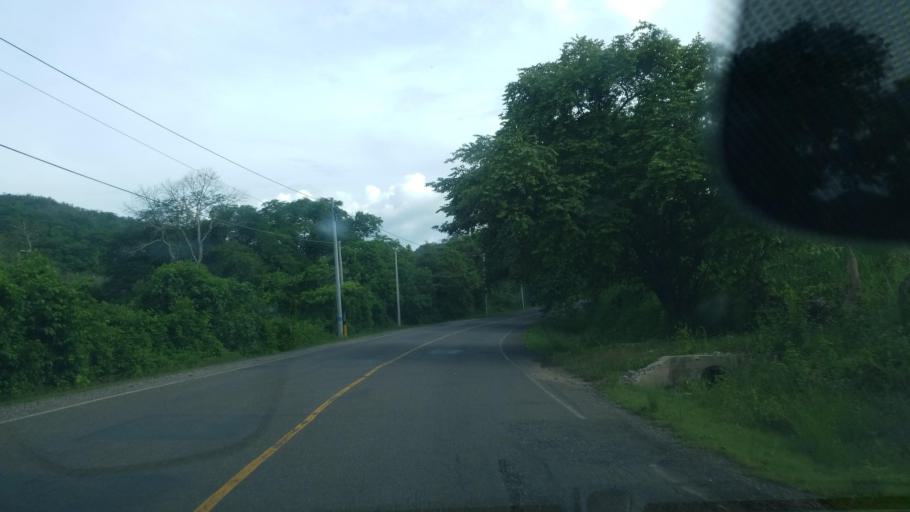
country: HN
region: Santa Barbara
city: Trinidad
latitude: 15.1171
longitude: -88.2012
